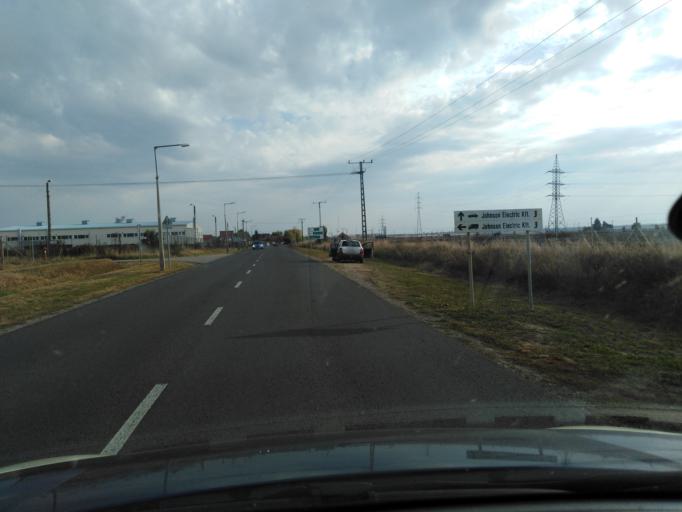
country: HU
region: Heves
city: Hatvan
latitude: 47.6650
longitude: 19.6430
